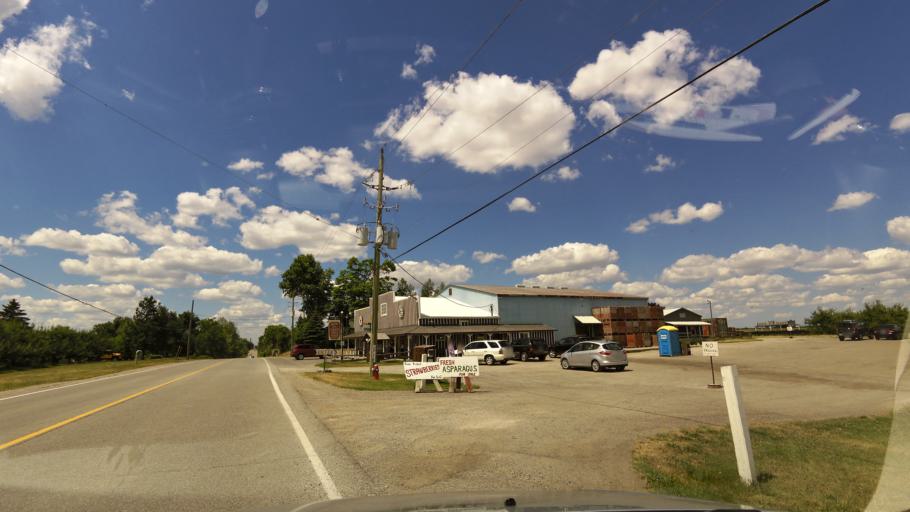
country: CA
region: Ontario
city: Brampton
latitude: 43.6290
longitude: -79.8016
